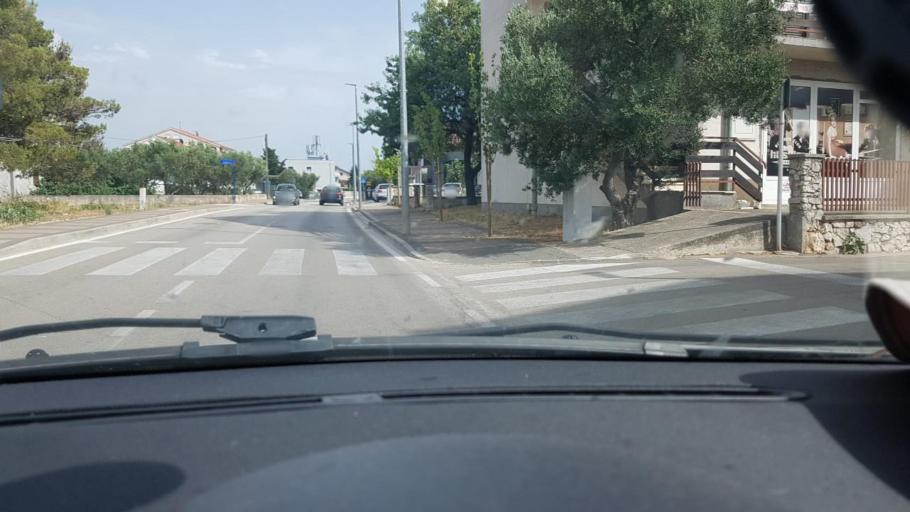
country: HR
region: Sibensko-Kniniska
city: Vodice
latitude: 43.7601
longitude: 15.7870
